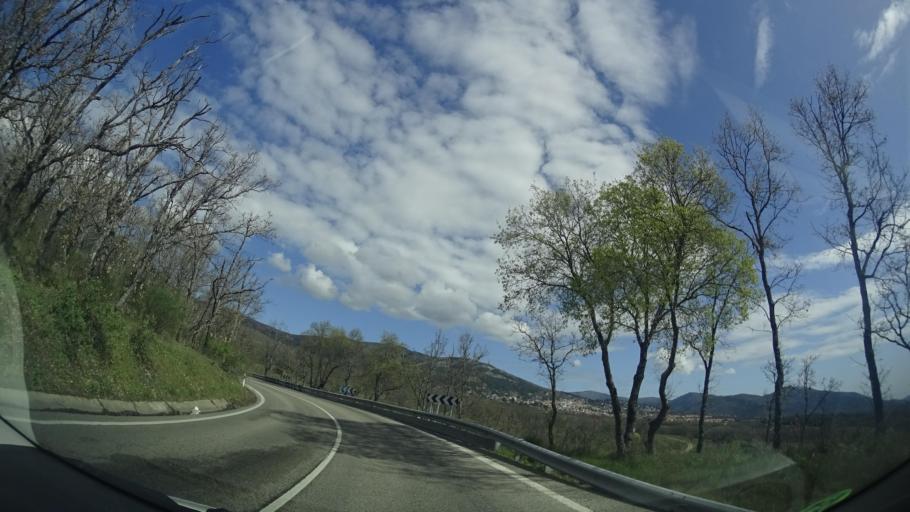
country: ES
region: Madrid
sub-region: Provincia de Madrid
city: Miraflores de la Sierra
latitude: 40.7903
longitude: -3.7730
